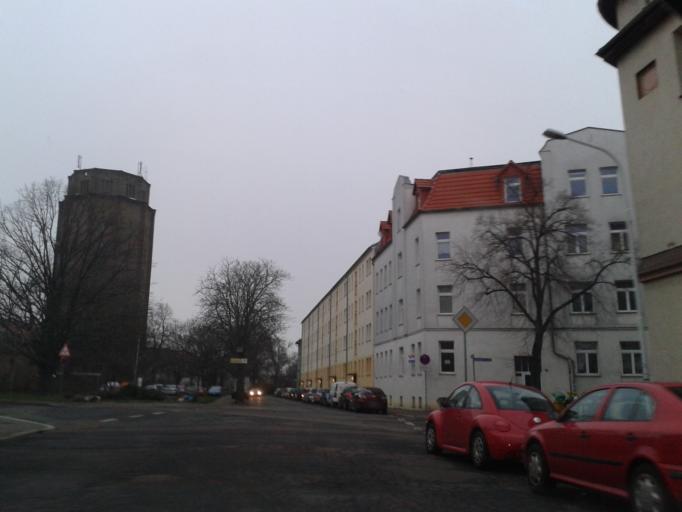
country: DE
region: Saxony-Anhalt
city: Halle (Saale)
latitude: 51.4651
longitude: 11.9786
